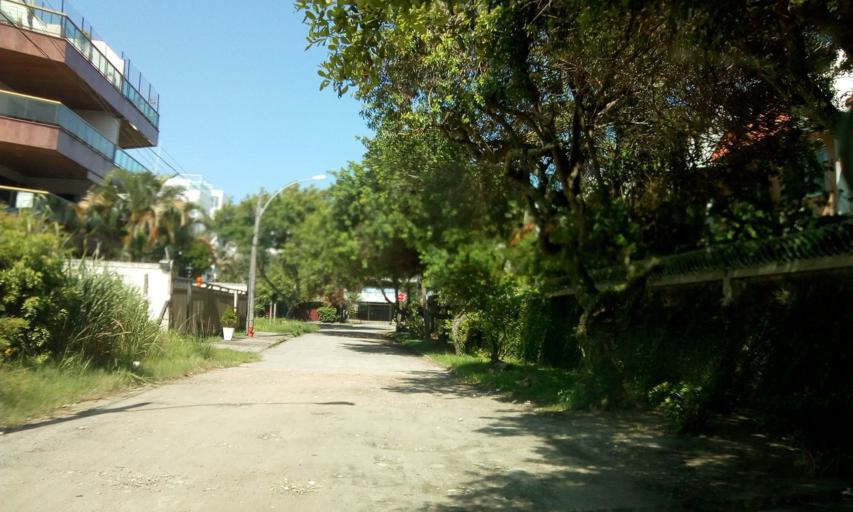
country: BR
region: Rio de Janeiro
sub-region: Nilopolis
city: Nilopolis
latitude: -23.0164
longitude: -43.4613
